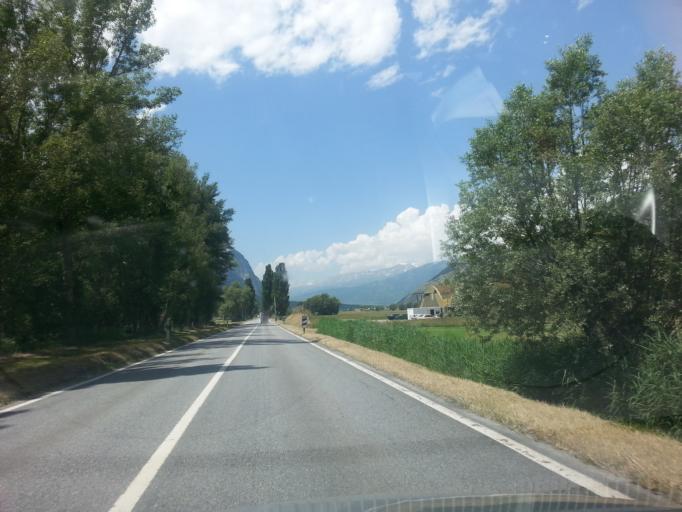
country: CH
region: Valais
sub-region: Leuk District
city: Gampel
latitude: 46.3047
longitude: 7.7290
